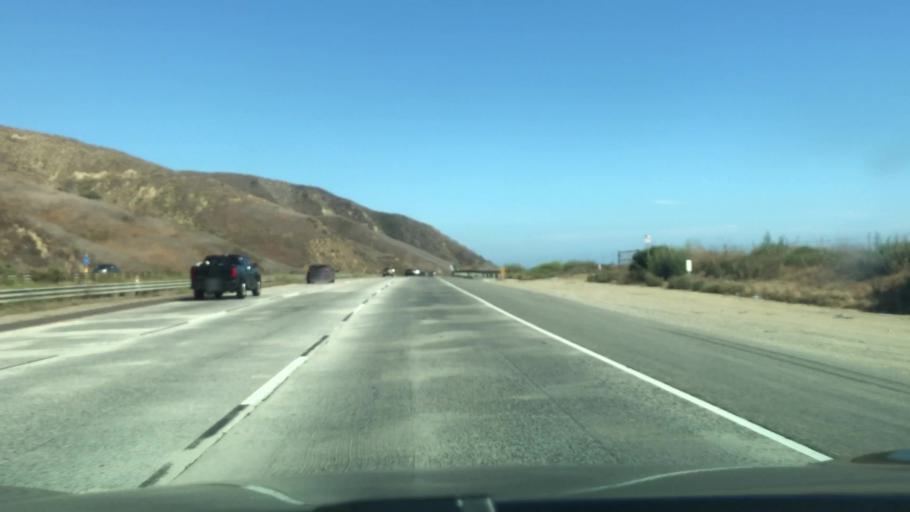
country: US
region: California
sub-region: Ventura County
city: Ventura
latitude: 34.3061
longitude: -119.3490
